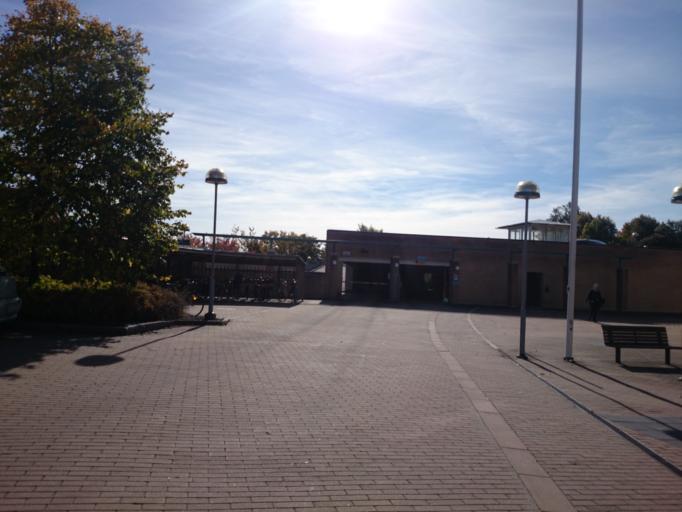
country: SE
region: Skane
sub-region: Lunds Kommun
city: Lund
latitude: 55.7082
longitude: 13.2201
